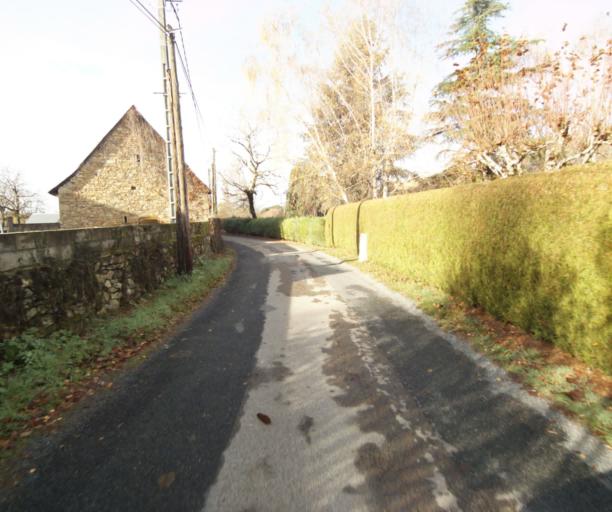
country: FR
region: Limousin
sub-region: Departement de la Correze
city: Sainte-Fortunade
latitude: 45.2232
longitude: 1.7453
